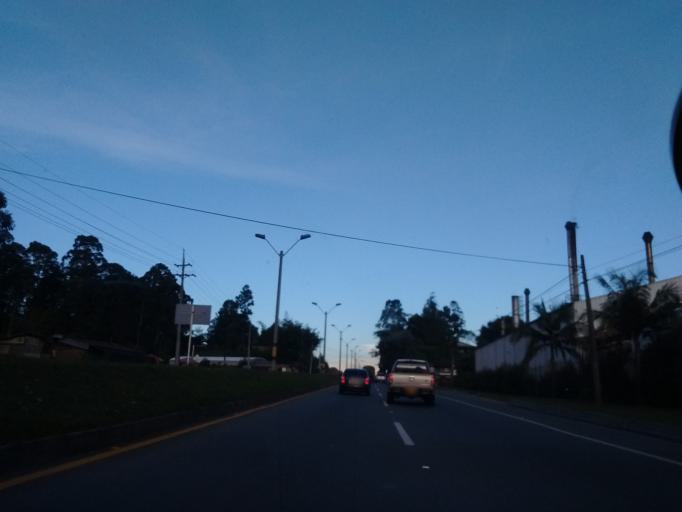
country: CO
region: Antioquia
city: Marinilla
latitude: 6.1775
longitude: -75.3580
